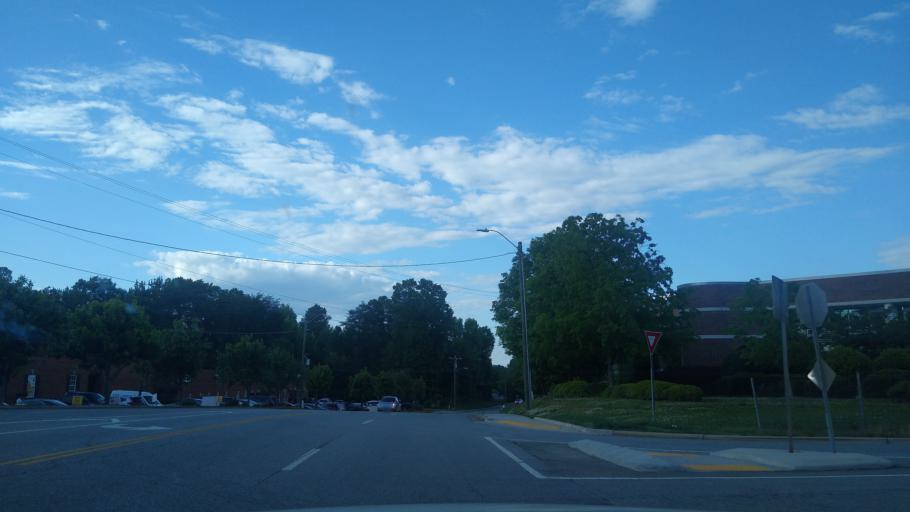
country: US
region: North Carolina
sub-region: Guilford County
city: Greensboro
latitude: 36.0885
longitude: -79.7824
